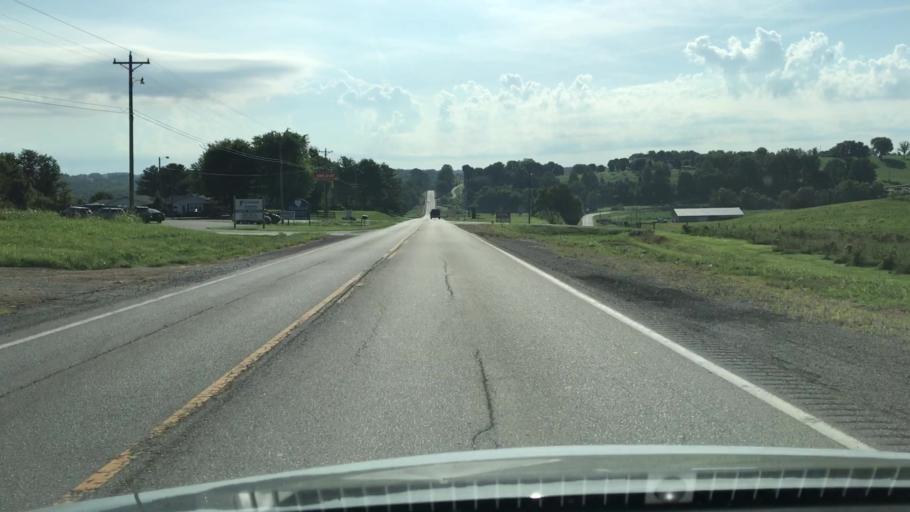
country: US
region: Kentucky
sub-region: Metcalfe County
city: Edmonton
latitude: 36.9884
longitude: -85.6522
